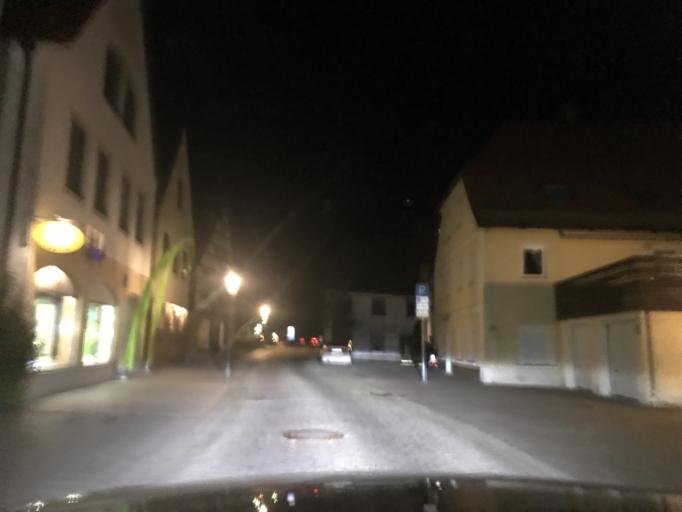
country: DE
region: Bavaria
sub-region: Upper Franconia
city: Ebermannstadt
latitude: 49.7809
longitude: 11.1885
